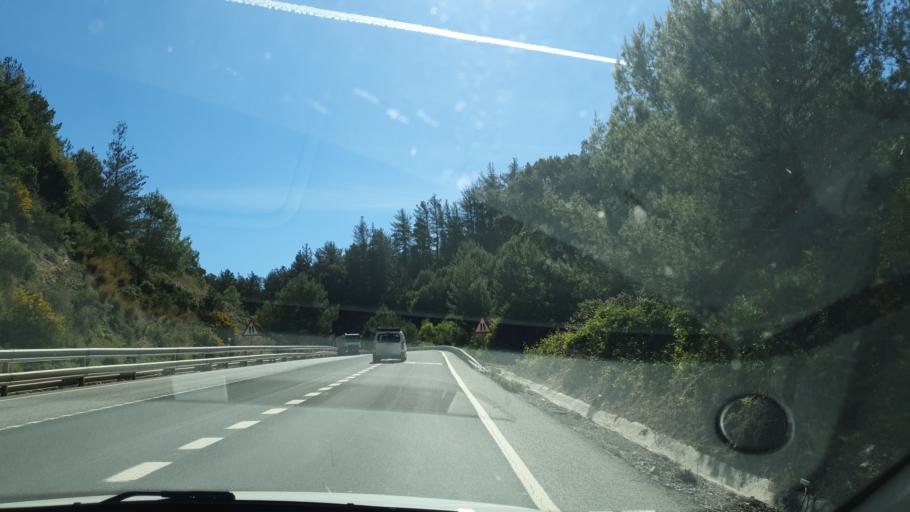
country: ES
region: Andalusia
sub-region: Provincia de Malaga
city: Ojen
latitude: 36.5747
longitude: -4.8606
